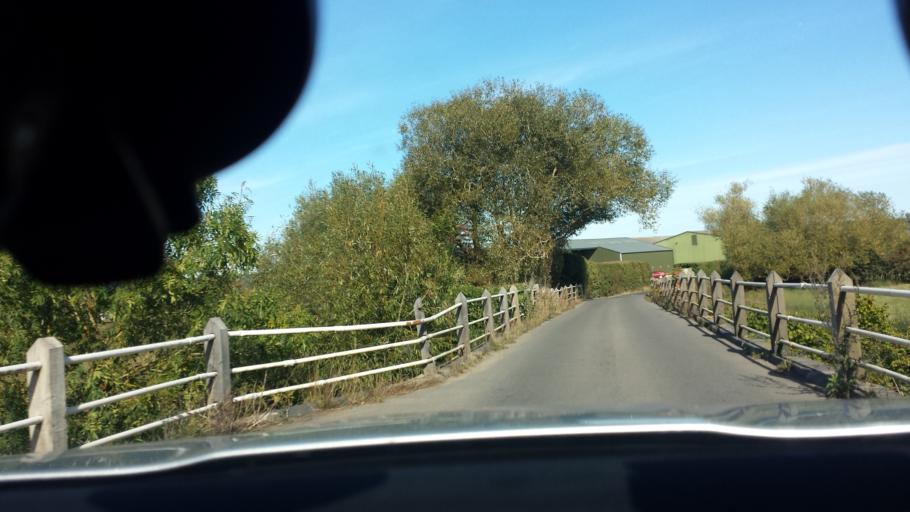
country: GB
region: England
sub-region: Kent
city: Staplehurst
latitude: 51.1921
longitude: 0.5495
